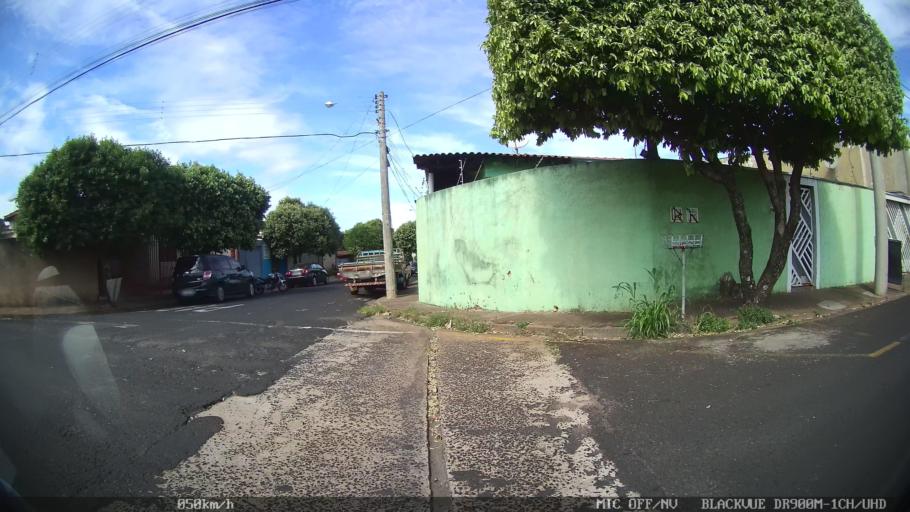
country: BR
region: Sao Paulo
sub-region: Sao Jose Do Rio Preto
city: Sao Jose do Rio Preto
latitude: -20.8351
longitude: -49.3518
